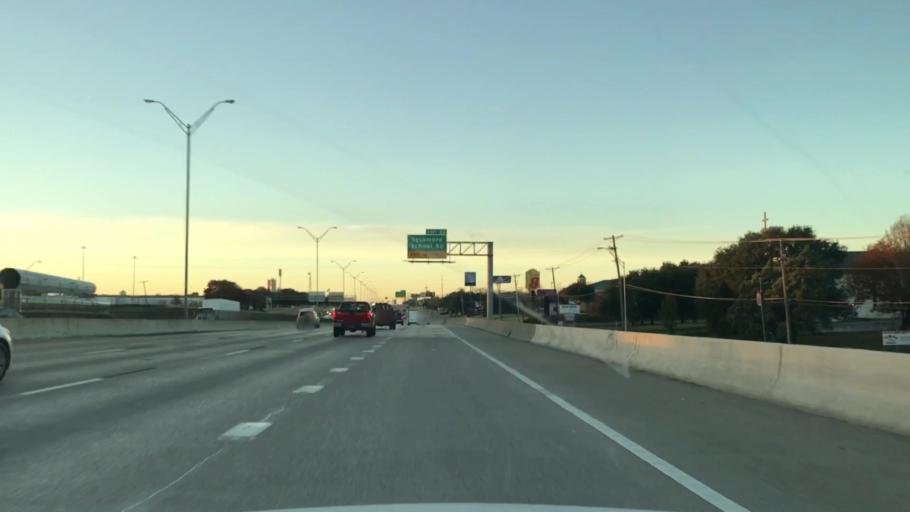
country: US
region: Texas
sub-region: Tarrant County
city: Edgecliff Village
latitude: 32.6532
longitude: -97.3215
